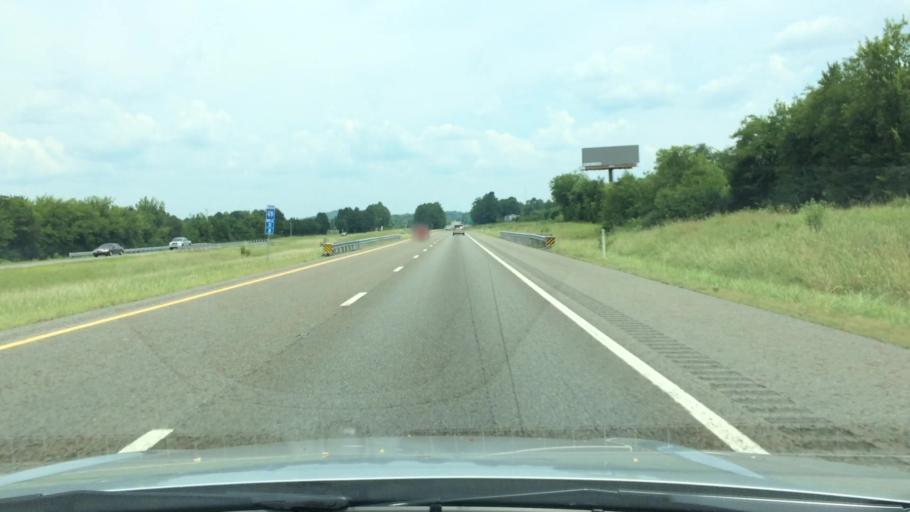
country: US
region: Tennessee
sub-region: Marshall County
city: Cornersville
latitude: 35.4384
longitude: -86.8814
